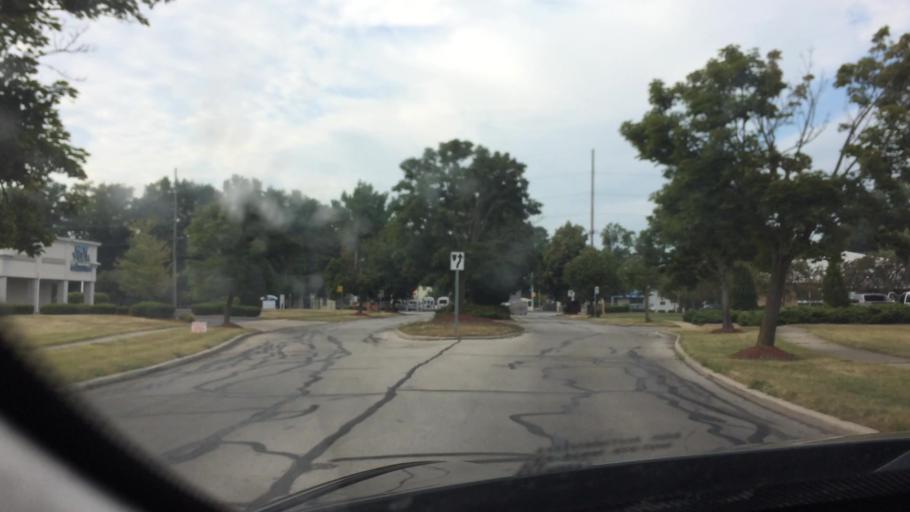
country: US
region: Ohio
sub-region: Lucas County
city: Ottawa Hills
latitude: 41.6520
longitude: -83.6571
